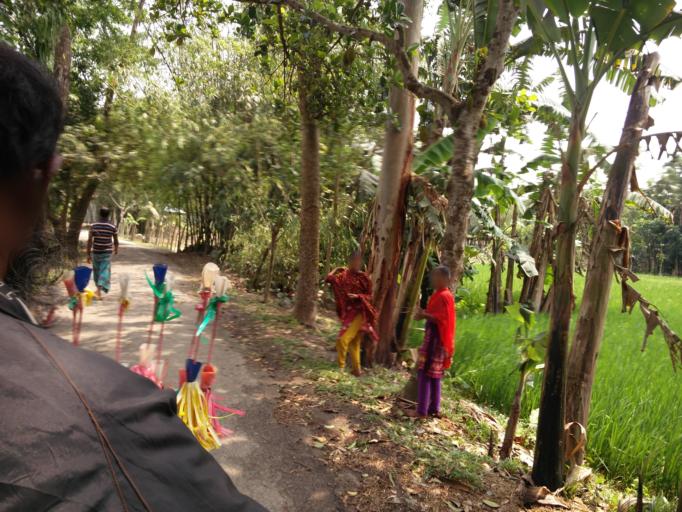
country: BD
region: Dhaka
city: Sherpur
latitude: 24.9341
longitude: 90.1598
